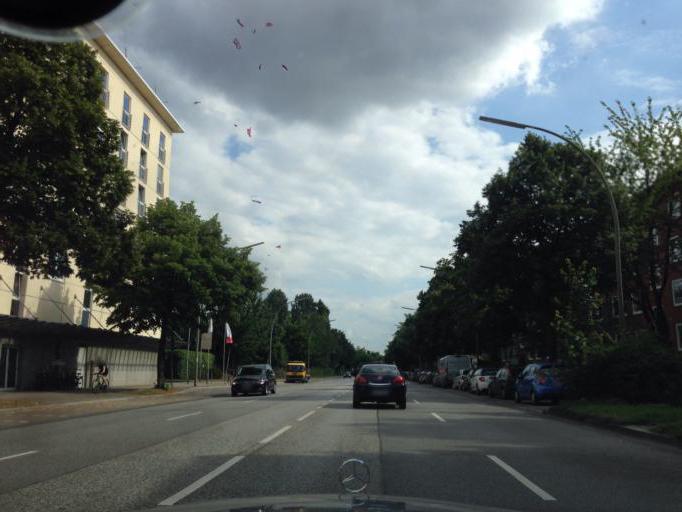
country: DE
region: Hamburg
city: Marienthal
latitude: 53.5590
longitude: 10.0813
